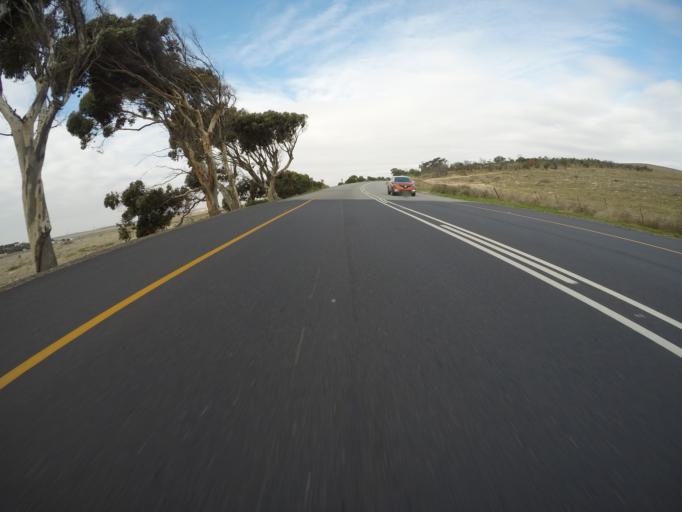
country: ZA
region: Western Cape
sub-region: City of Cape Town
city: Sunset Beach
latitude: -33.7252
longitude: 18.4723
